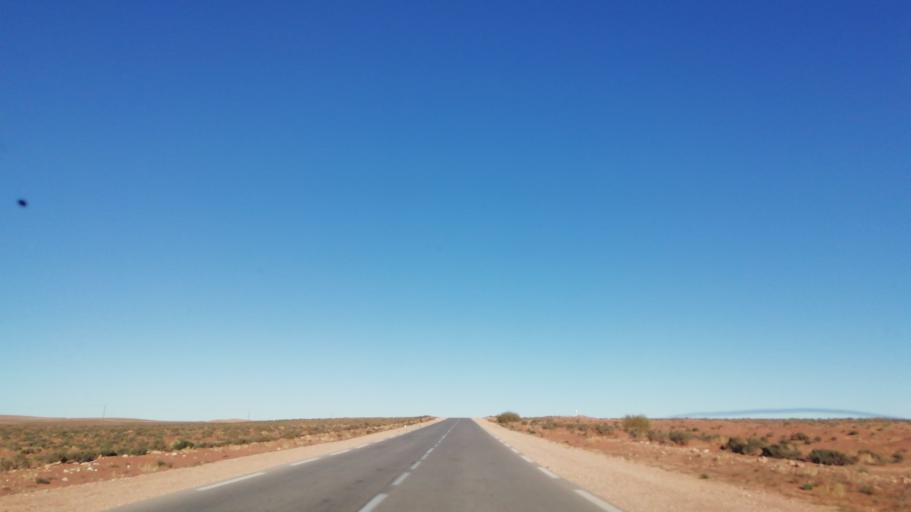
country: DZ
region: El Bayadh
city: El Abiodh Sidi Cheikh
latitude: 33.1232
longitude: 0.2778
